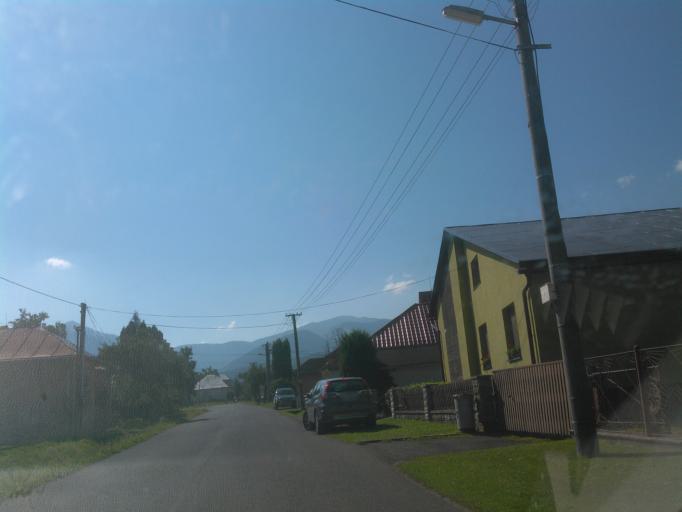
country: SK
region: Zilinsky
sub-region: Okres Liptovsky Mikulas
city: Liptovsky Mikulas
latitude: 49.0372
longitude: 19.5002
